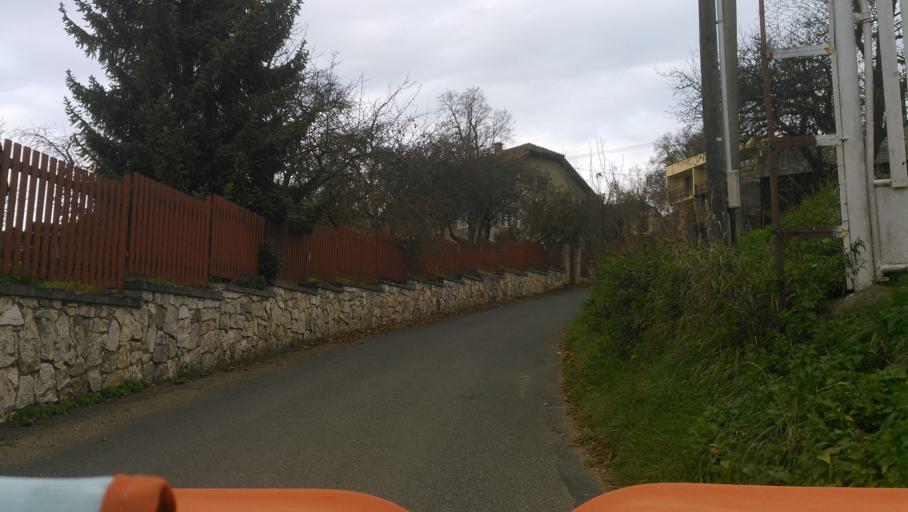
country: SK
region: Presovsky
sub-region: Okres Presov
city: Levoca
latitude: 49.0301
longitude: 20.5955
